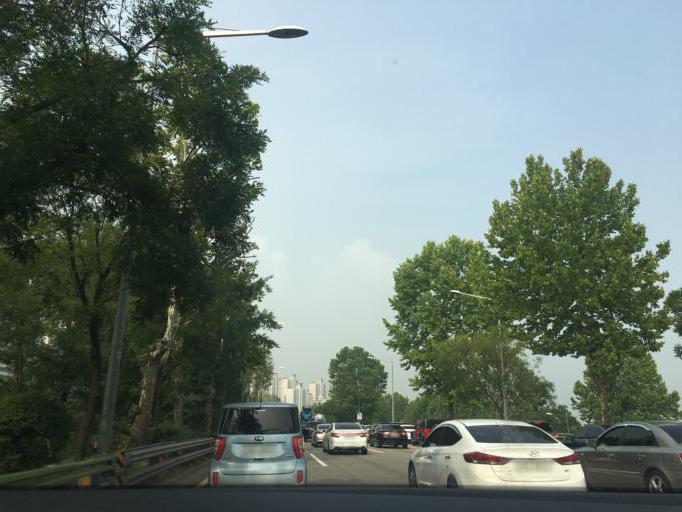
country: KR
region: Gyeonggi-do
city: Seongnam-si
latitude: 37.5187
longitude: 127.0934
